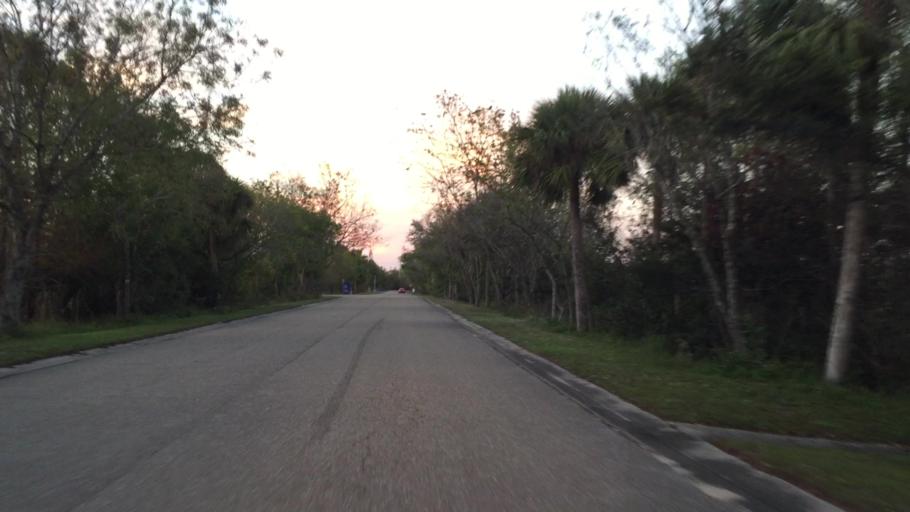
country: US
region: Florida
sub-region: Lee County
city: Gateway
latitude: 26.5346
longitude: -81.7915
